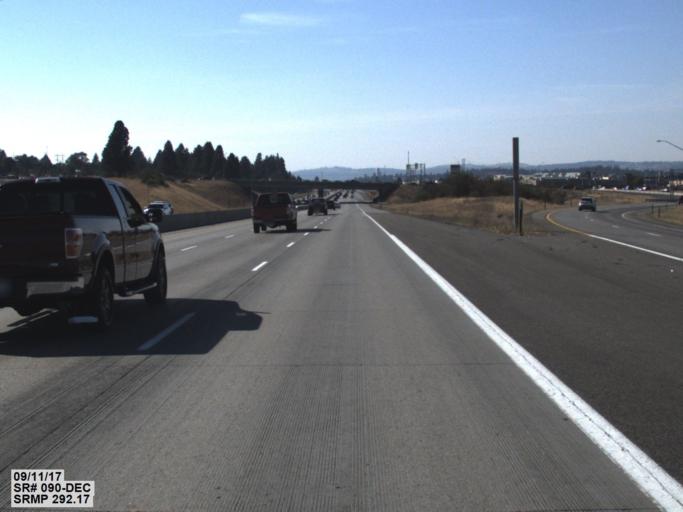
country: US
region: Washington
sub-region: Spokane County
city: Veradale
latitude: 47.6683
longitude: -117.1913
